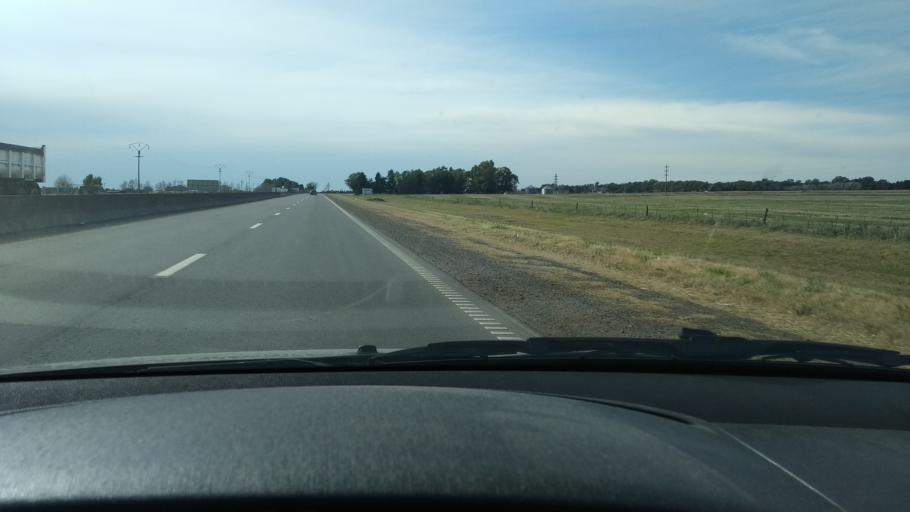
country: AR
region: Buenos Aires
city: Olavarria
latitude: -36.9077
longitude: -60.1935
